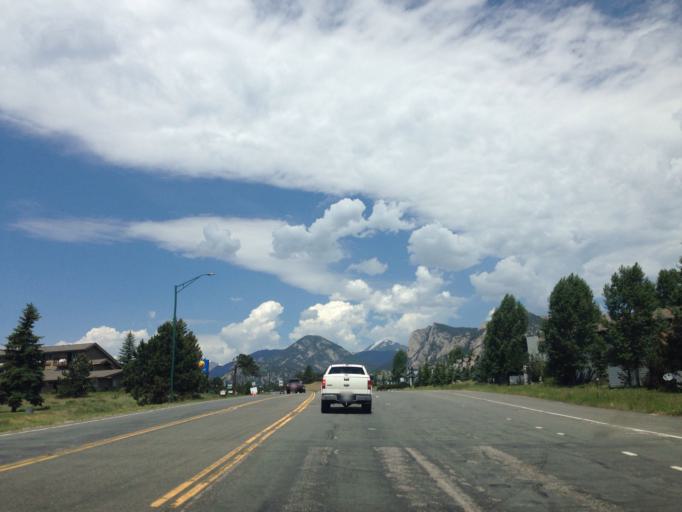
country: US
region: Colorado
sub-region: Larimer County
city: Estes Park
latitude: 40.3819
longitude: -105.4962
